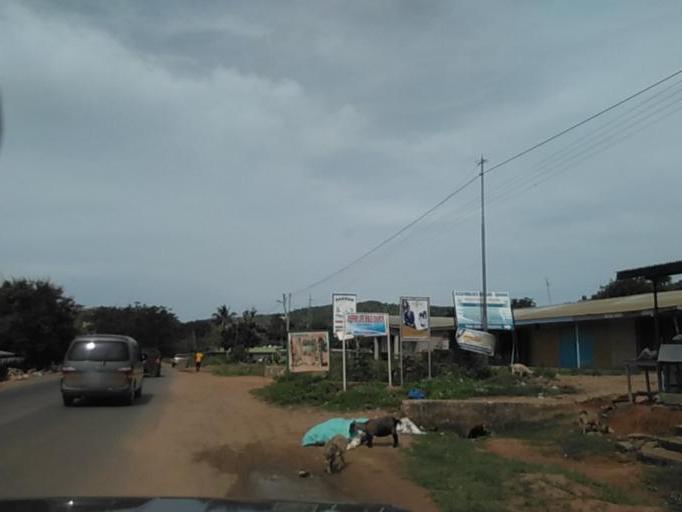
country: GH
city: Akropong
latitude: 6.2286
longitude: 0.0892
